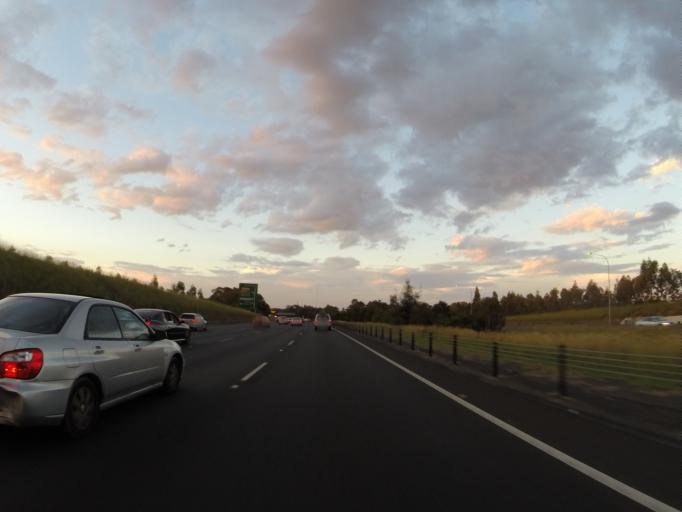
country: AU
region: New South Wales
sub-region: Campbelltown Municipality
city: Glenfield
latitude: -33.9716
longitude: 150.8736
